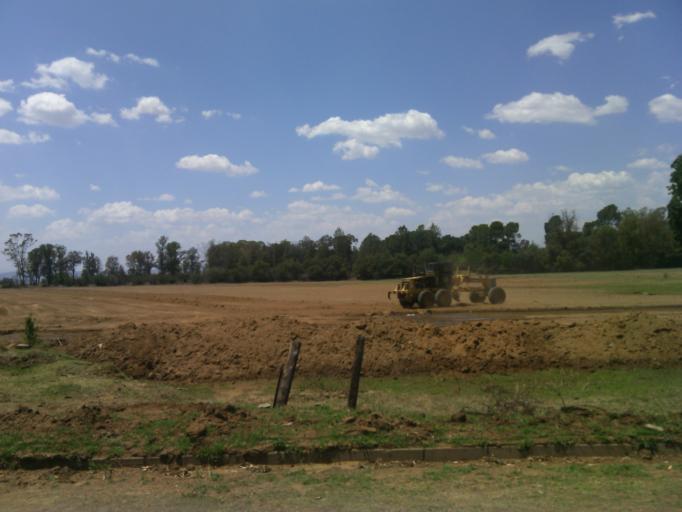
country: ZA
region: Orange Free State
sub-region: Xhariep District Municipality
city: Dewetsdorp
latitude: -29.5769
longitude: 26.6671
